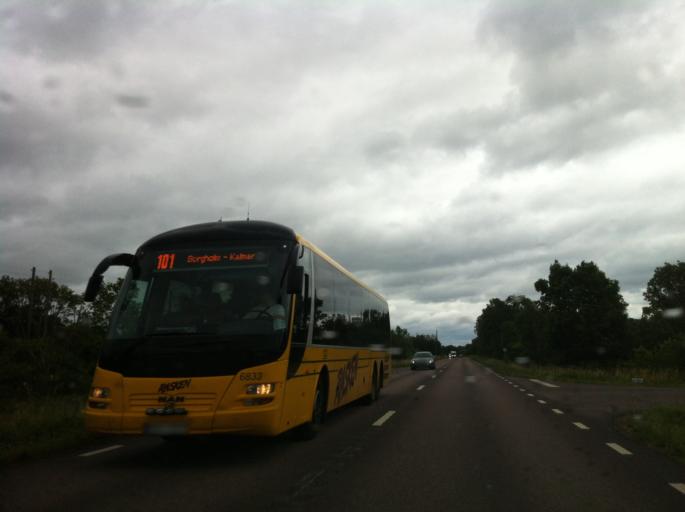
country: SE
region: Kalmar
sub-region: Borgholms Kommun
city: Borgholm
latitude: 57.1363
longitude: 16.9840
